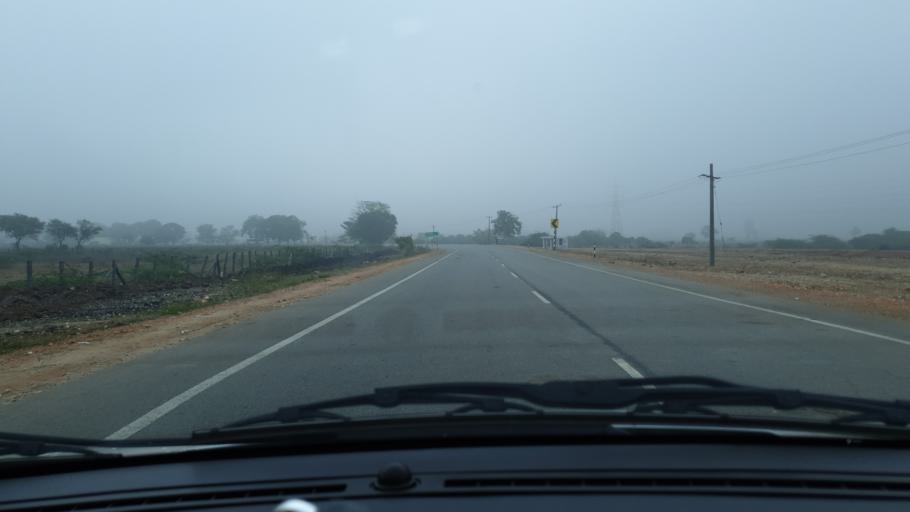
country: IN
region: Telangana
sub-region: Nalgonda
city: Devarkonda
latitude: 16.6313
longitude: 78.6085
